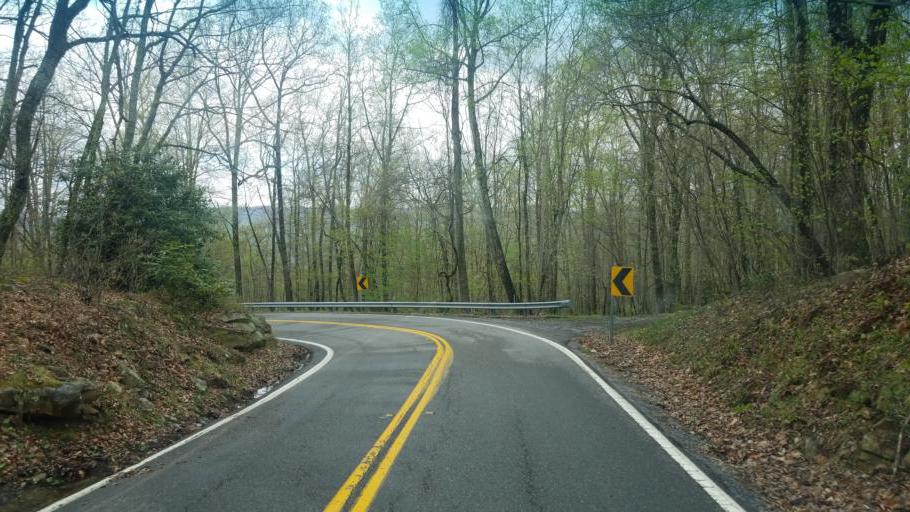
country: US
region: Virginia
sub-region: Tazewell County
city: Tazewell
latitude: 36.9947
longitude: -81.5336
